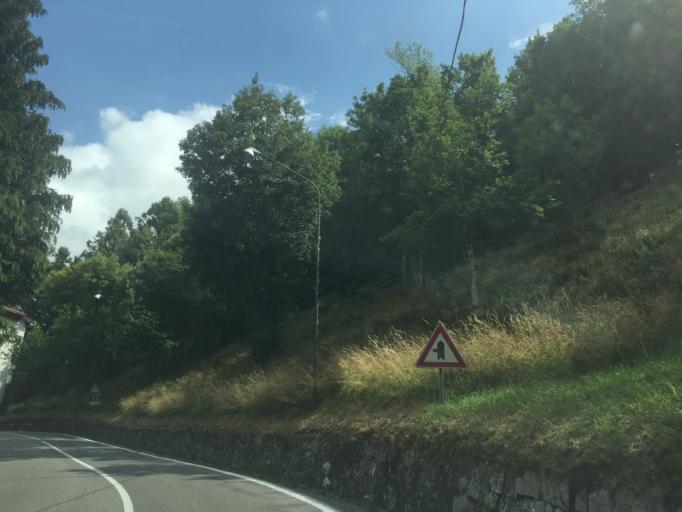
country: IT
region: Tuscany
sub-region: Provincia di Pistoia
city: Cutigliano
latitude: 44.1200
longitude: 10.7272
